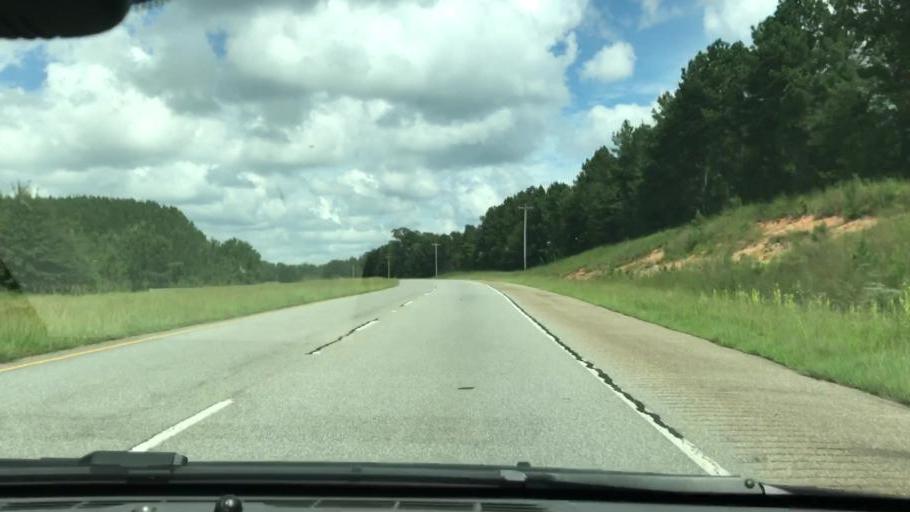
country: US
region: Georgia
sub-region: Stewart County
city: Lumpkin
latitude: 32.1131
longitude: -84.8140
